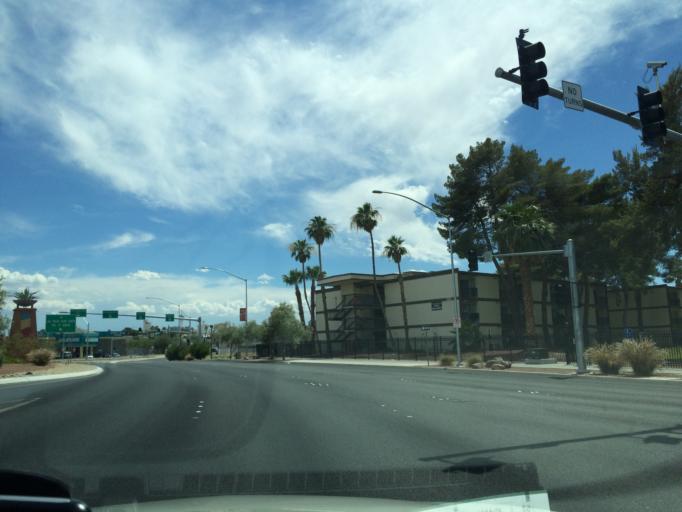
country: US
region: Nevada
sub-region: Clark County
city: Las Vegas
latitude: 36.1912
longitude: -115.1339
